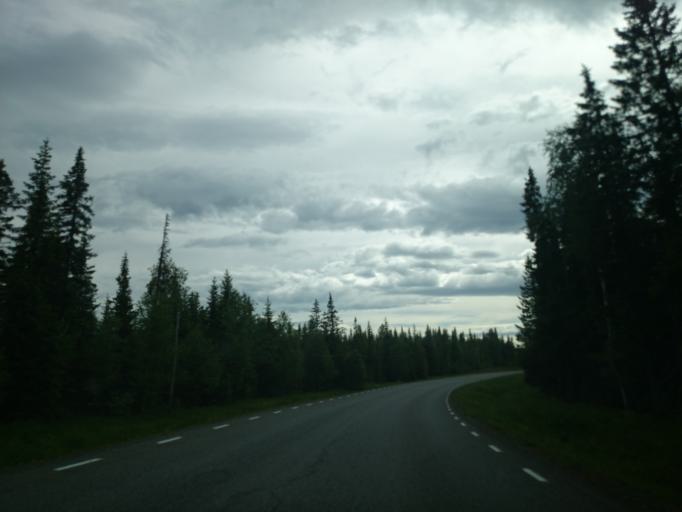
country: SE
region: Jaemtland
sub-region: Are Kommun
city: Are
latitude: 63.2054
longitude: 13.1618
